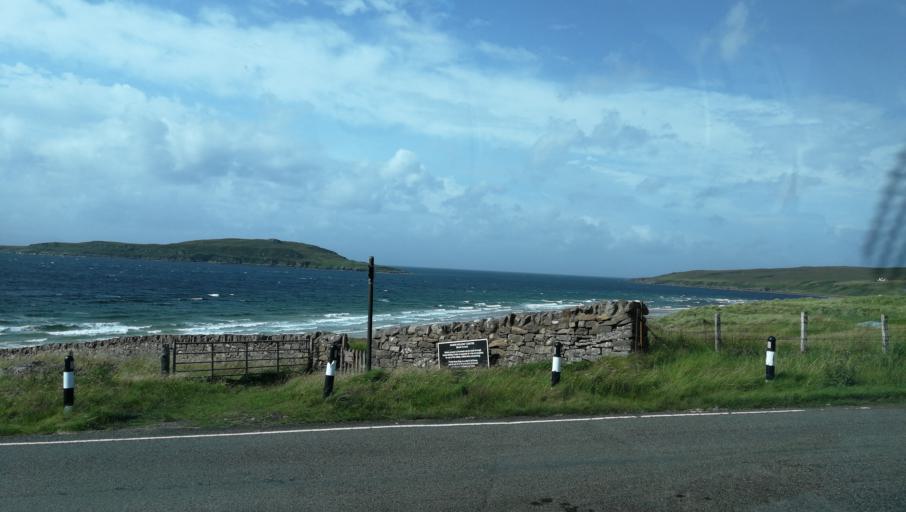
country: GB
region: Scotland
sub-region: Highland
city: Portree
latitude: 57.7348
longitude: -5.7635
